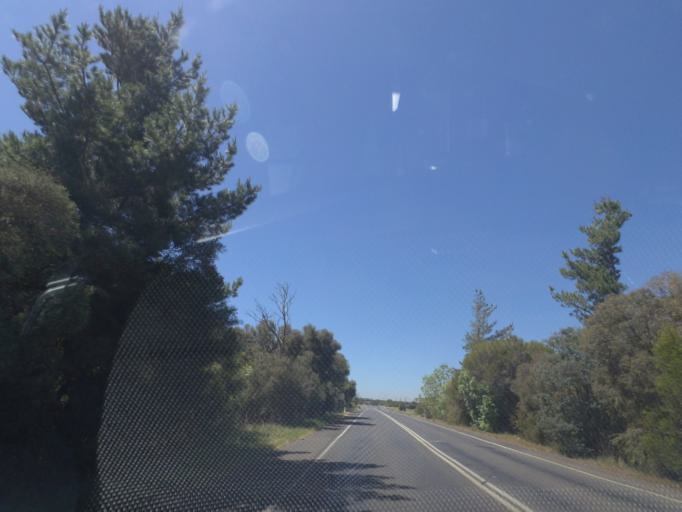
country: AU
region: Victoria
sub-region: Hume
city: Sunbury
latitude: -37.4259
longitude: 144.7249
